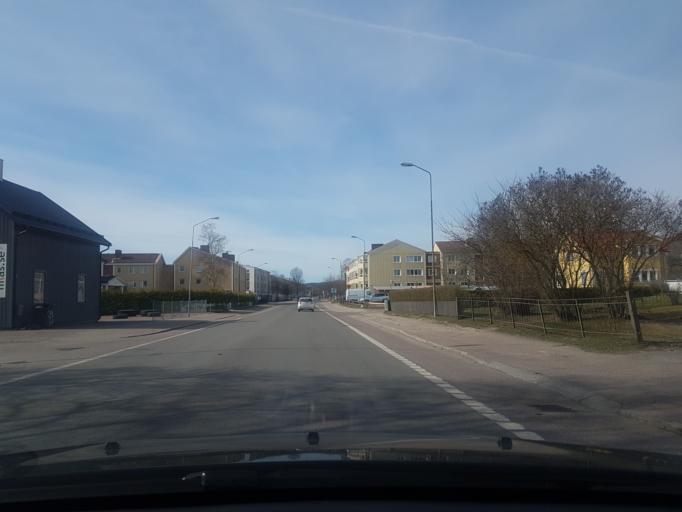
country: SE
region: Dalarna
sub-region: Borlange Kommun
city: Borlaenge
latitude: 60.4909
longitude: 15.4234
